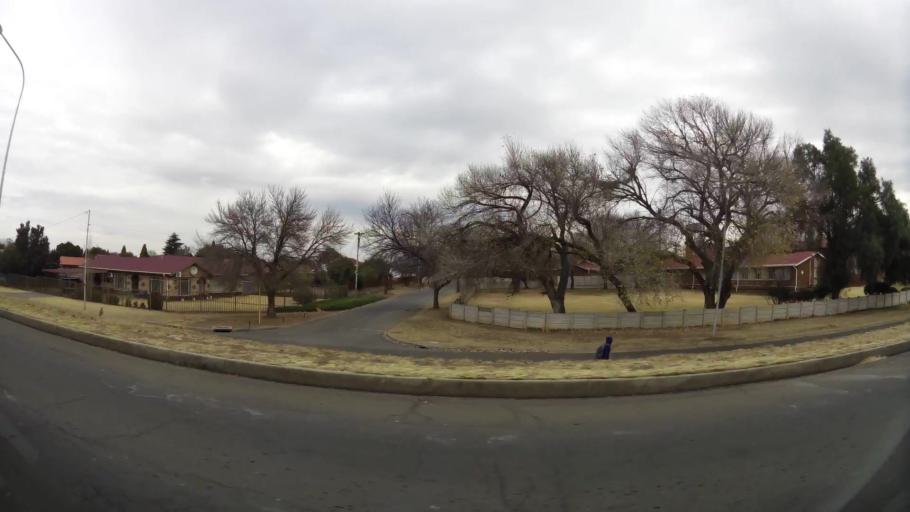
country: ZA
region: Orange Free State
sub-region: Fezile Dabi District Municipality
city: Kroonstad
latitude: -27.6405
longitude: 27.2334
